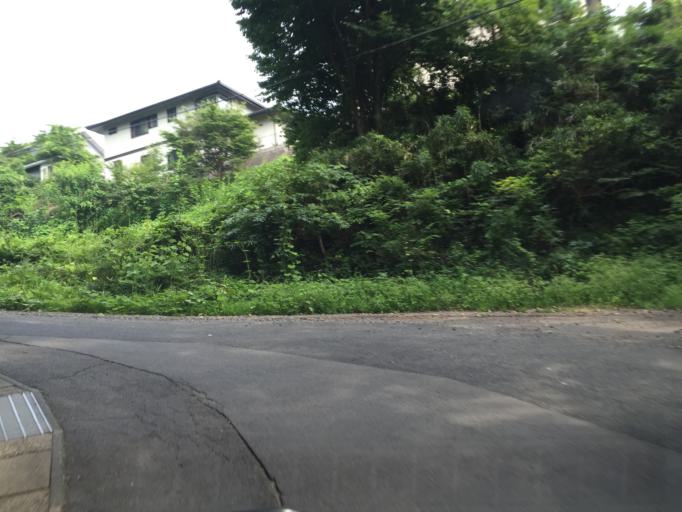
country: JP
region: Fukushima
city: Fukushima-shi
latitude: 37.7283
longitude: 140.4813
